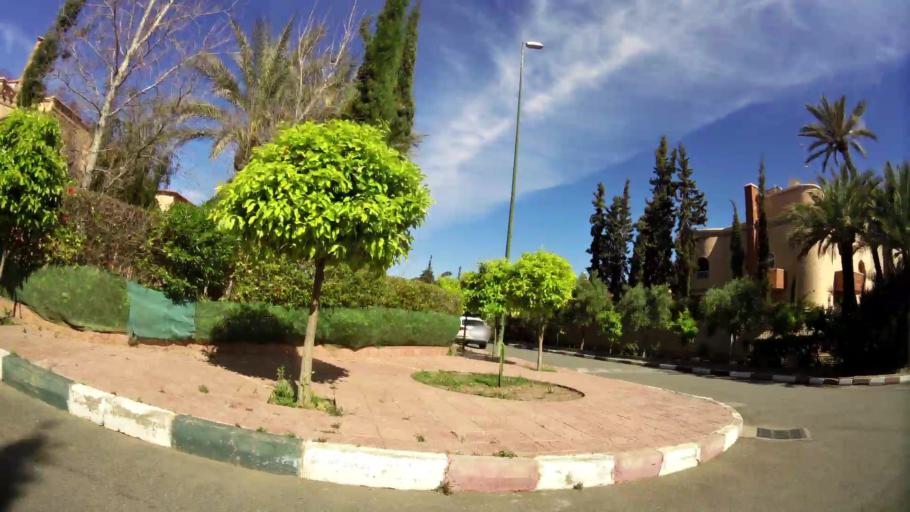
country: MA
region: Marrakech-Tensift-Al Haouz
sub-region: Marrakech
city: Marrakesh
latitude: 31.6545
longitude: -8.0562
